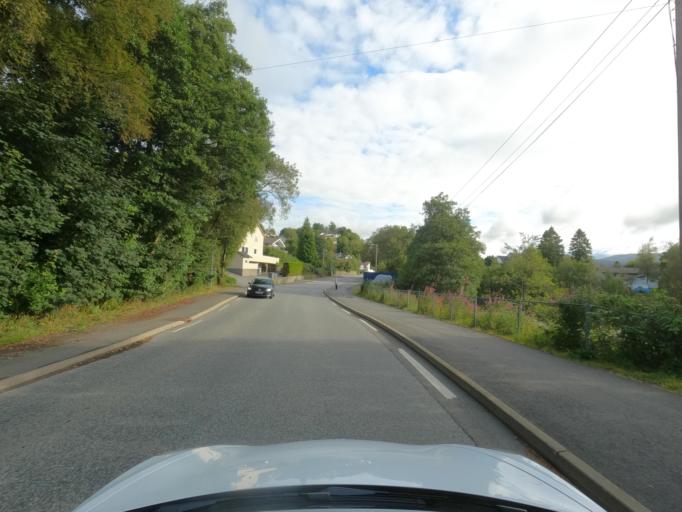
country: NO
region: Hordaland
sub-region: Bergen
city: Sandsli
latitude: 60.3009
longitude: 5.3459
